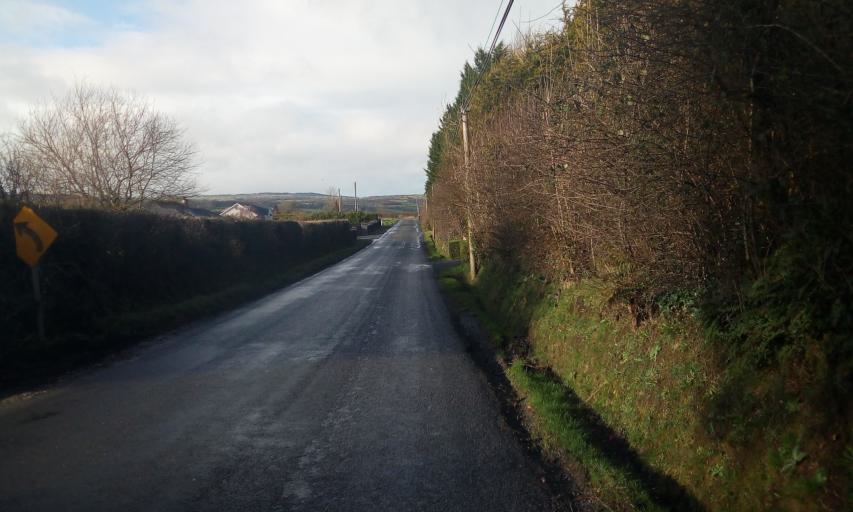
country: IE
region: Leinster
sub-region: Kilkenny
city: Castlecomer
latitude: 52.8019
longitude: -7.1921
